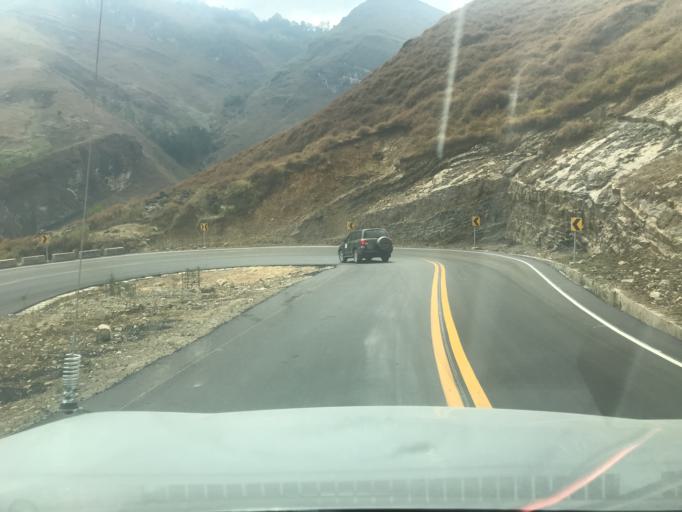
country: TL
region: Manufahi
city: Same
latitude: -8.8934
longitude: 125.5906
